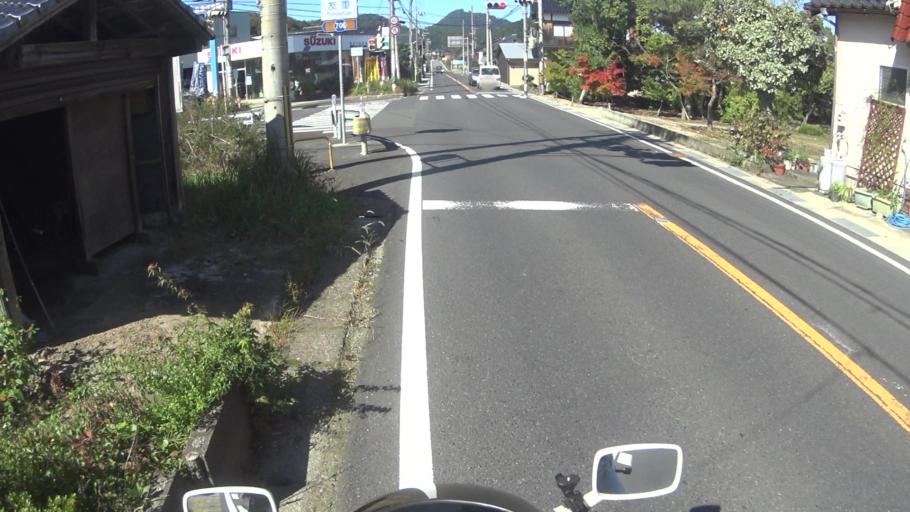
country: JP
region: Hyogo
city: Toyooka
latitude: 35.5887
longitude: 134.9250
